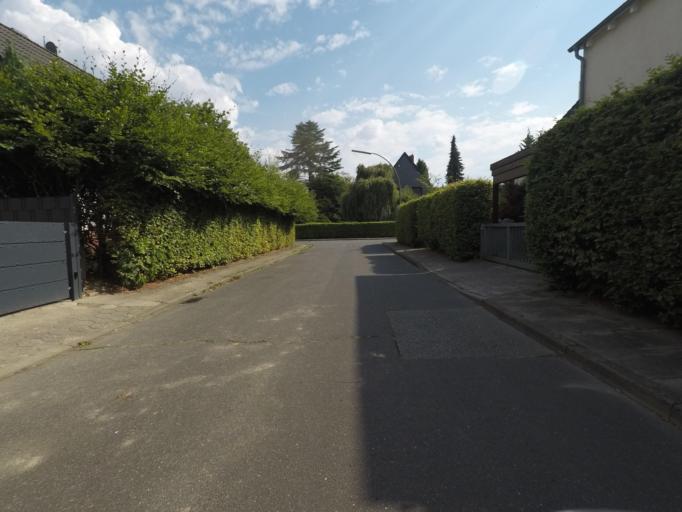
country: DE
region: Hamburg
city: Wellingsbuettel
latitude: 53.6524
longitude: 10.0667
